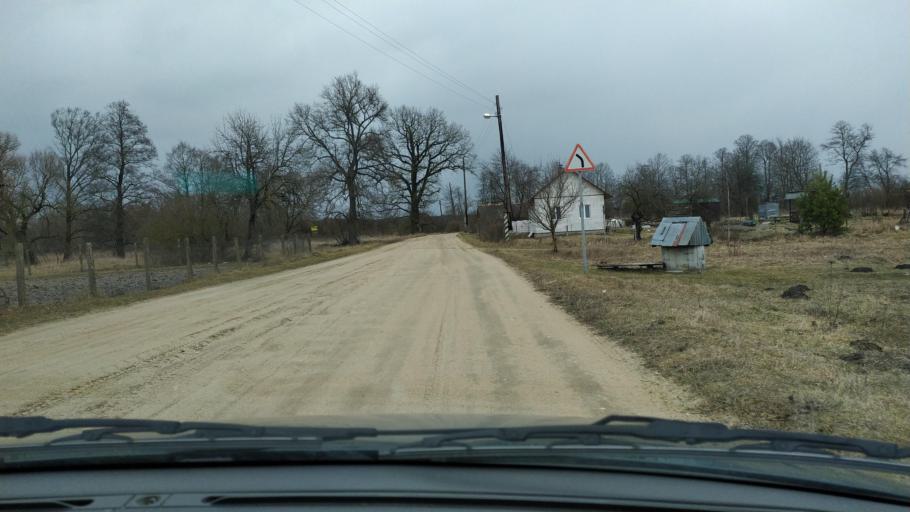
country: BY
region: Brest
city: Kamyanyets
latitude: 52.4043
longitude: 24.0096
